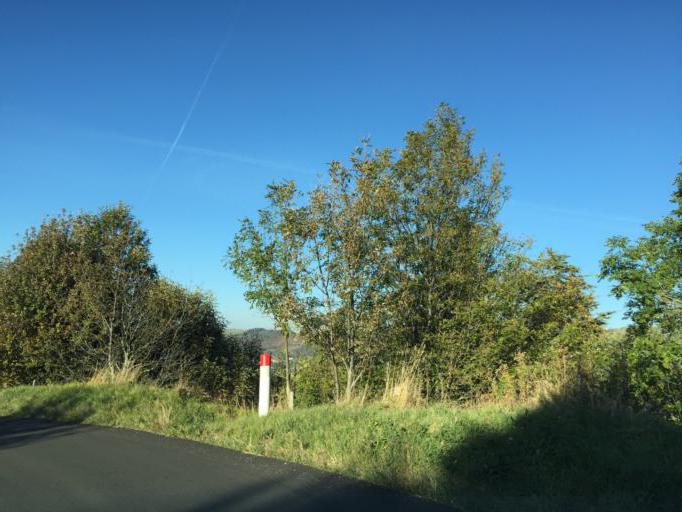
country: FR
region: Rhone-Alpes
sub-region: Departement de la Loire
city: Saint-Chamond
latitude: 45.4095
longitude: 4.5297
